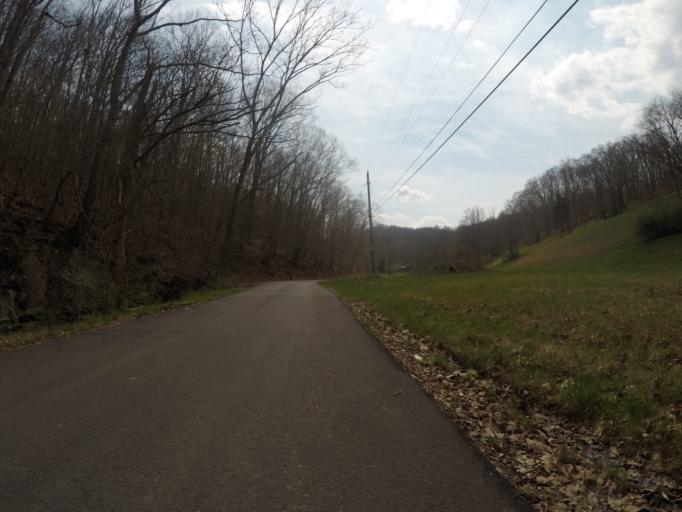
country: US
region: West Virginia
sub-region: Cabell County
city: Pea Ridge
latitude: 38.3983
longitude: -82.3510
